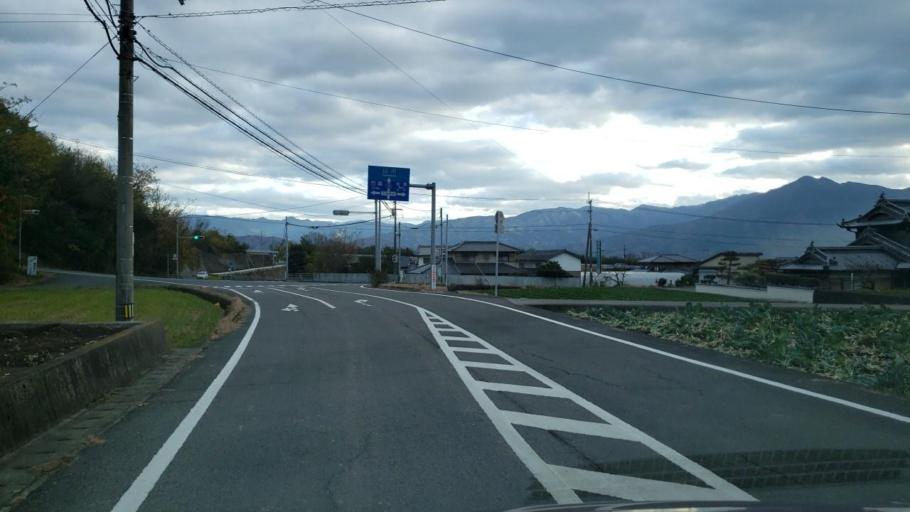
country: JP
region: Tokushima
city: Wakimachi
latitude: 34.1018
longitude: 134.2255
